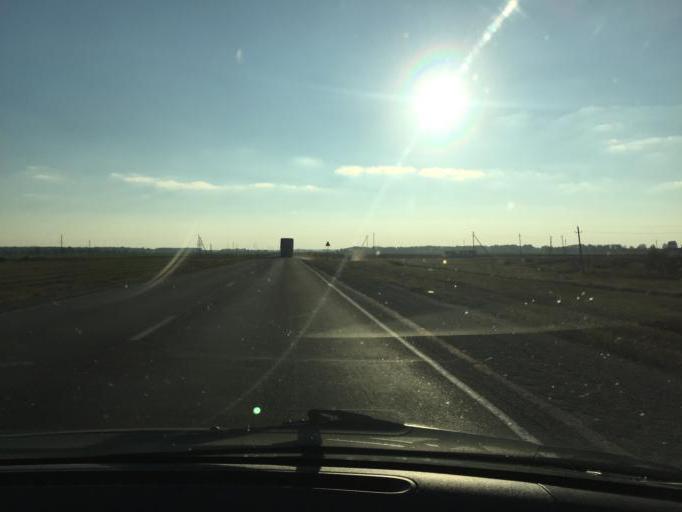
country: BY
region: Brest
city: Asnyezhytsy
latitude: 52.2826
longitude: 26.4055
